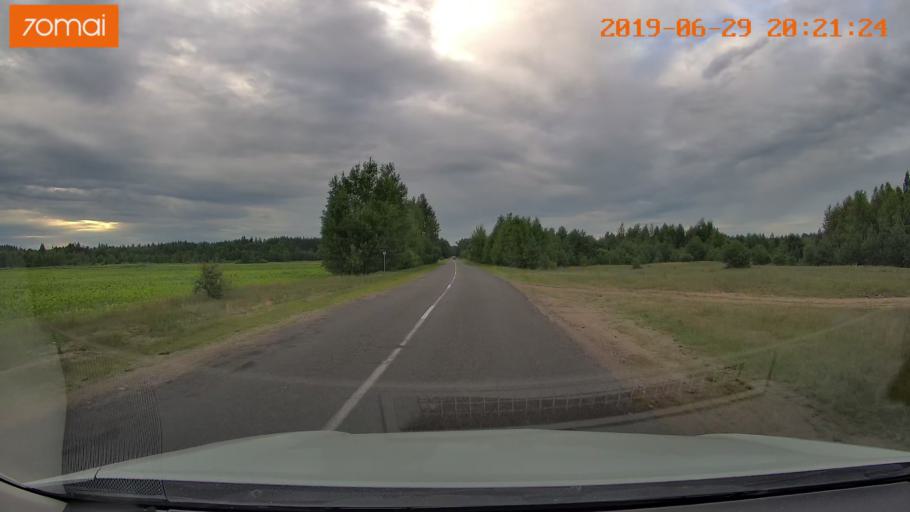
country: BY
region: Brest
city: Asnyezhytsy
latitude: 52.4194
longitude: 26.2529
